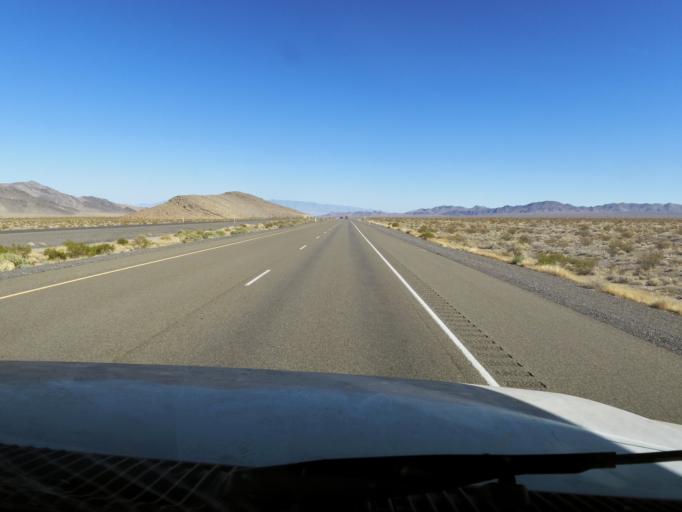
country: US
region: Nevada
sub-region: Nye County
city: Pahrump
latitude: 36.5712
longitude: -115.8647
